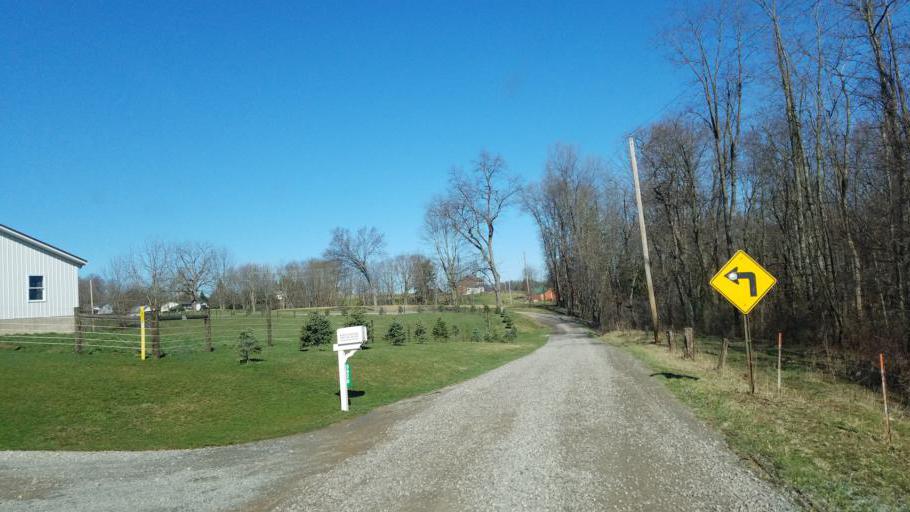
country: US
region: Ohio
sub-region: Wayne County
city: Apple Creek
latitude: 40.6668
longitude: -81.8282
